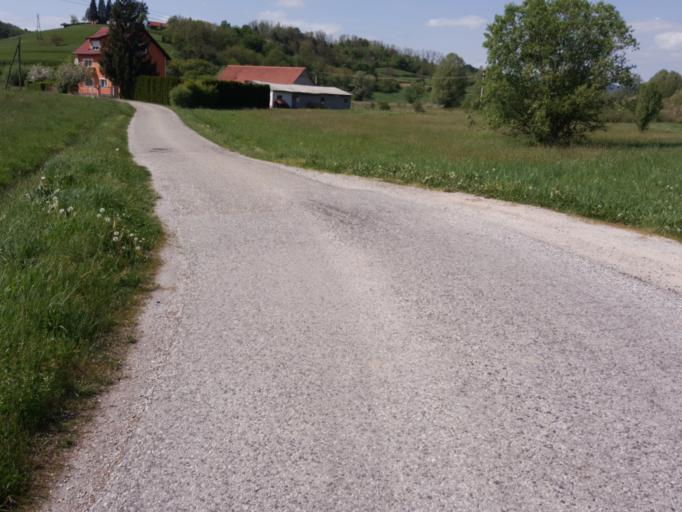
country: HR
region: Varazdinska
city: Lepoglava
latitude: 46.2288
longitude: 15.9652
